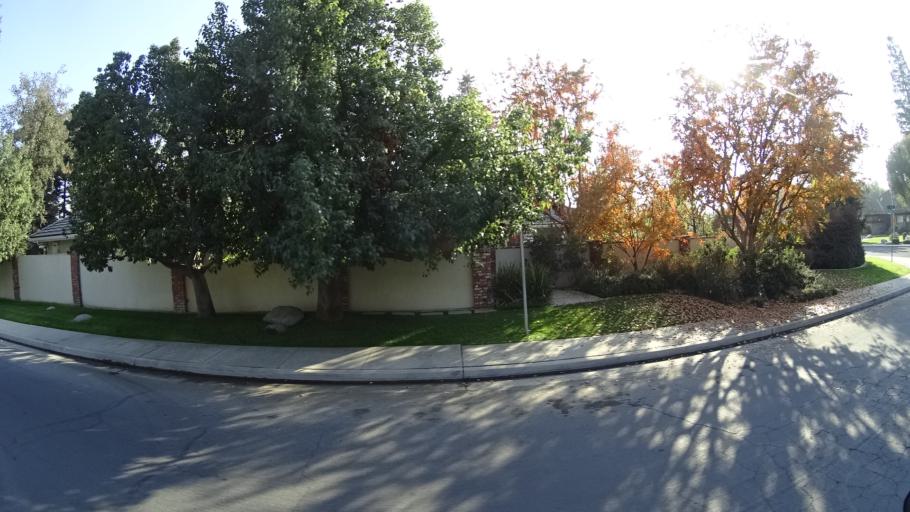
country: US
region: California
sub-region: Kern County
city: Rosedale
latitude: 35.3566
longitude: -119.1507
